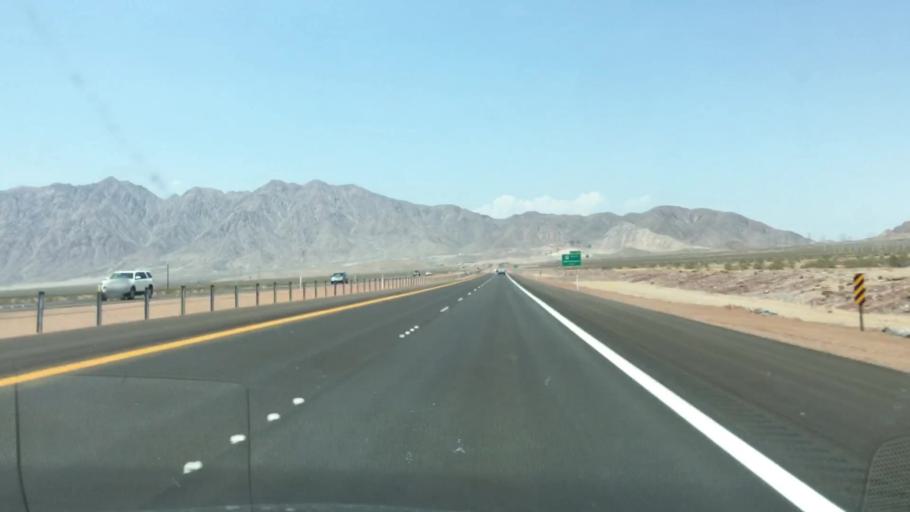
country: US
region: Nevada
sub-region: Clark County
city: Boulder City
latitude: 35.9421
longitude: -114.8796
